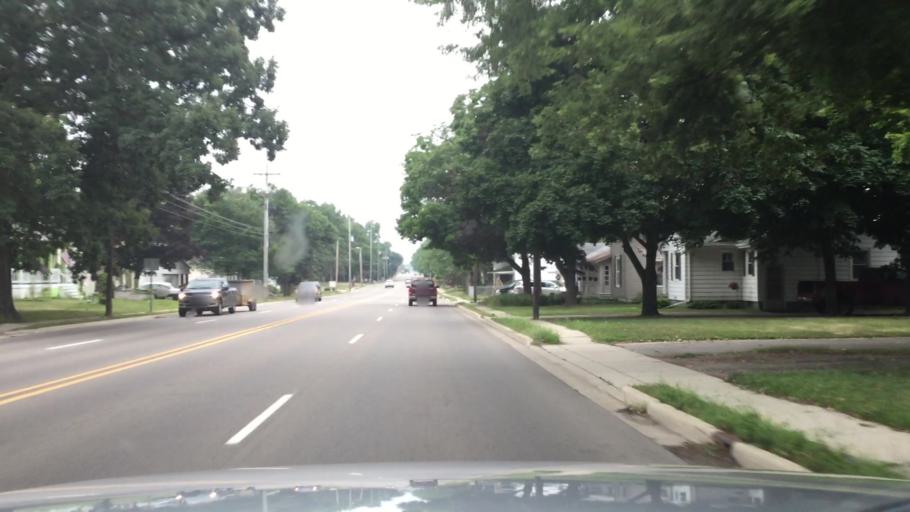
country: US
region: Michigan
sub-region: Shiawassee County
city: Owosso
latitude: 43.0113
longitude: -84.1768
